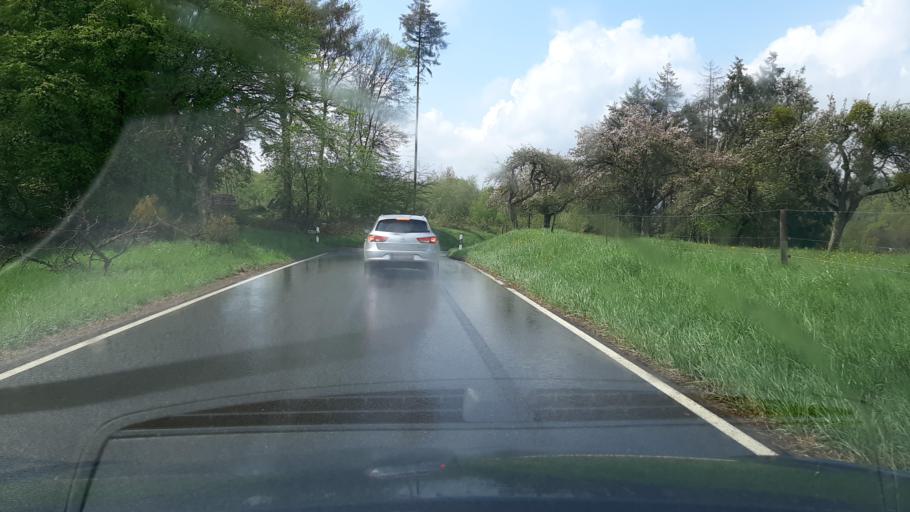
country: DE
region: Rheinland-Pfalz
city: Alken
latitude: 50.2499
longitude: 7.4758
